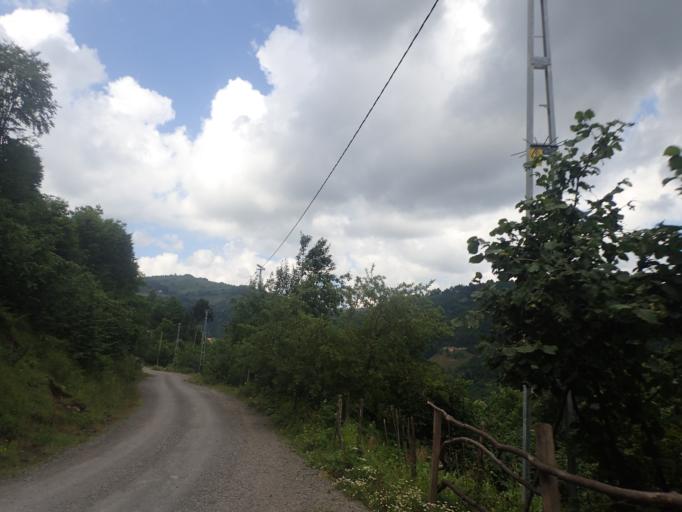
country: TR
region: Ordu
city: Akkus
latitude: 40.8986
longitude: 37.0097
